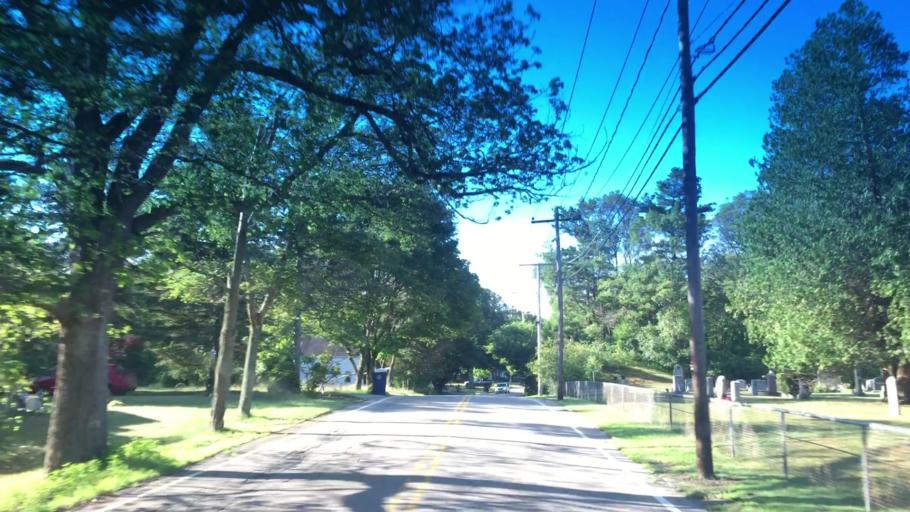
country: US
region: Massachusetts
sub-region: Norfolk County
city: Medway
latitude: 42.1494
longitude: -71.3918
